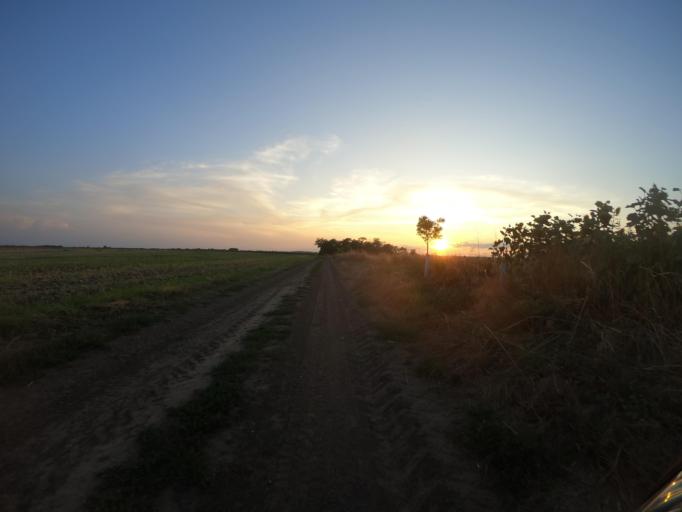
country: HU
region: Borsod-Abauj-Zemplen
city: Szentistvan
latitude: 47.7455
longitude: 20.7254
